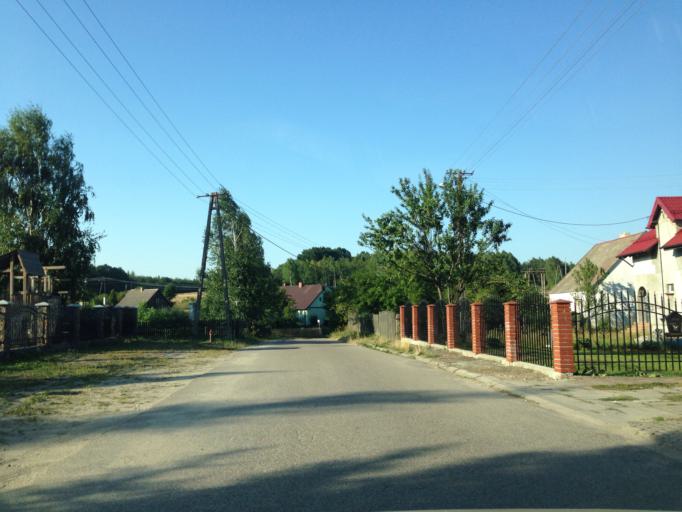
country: PL
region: Warmian-Masurian Voivodeship
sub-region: Powiat dzialdowski
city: Lidzbark
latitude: 53.2390
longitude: 19.7524
